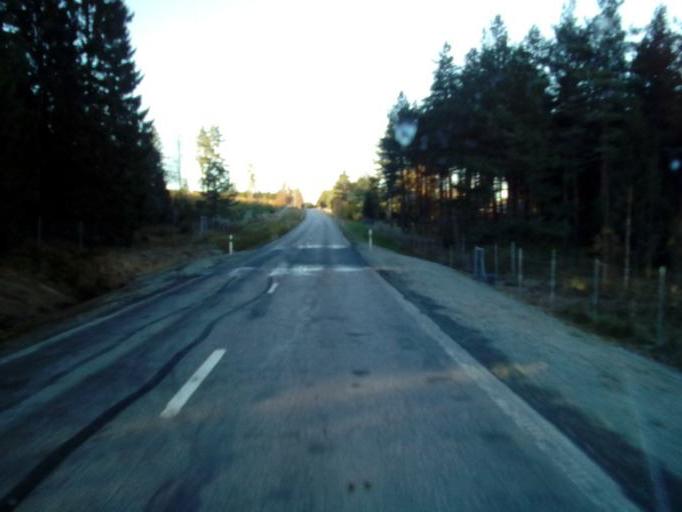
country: SE
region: OErebro
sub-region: Hallsbergs Kommun
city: Palsboda
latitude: 58.9206
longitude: 15.4332
